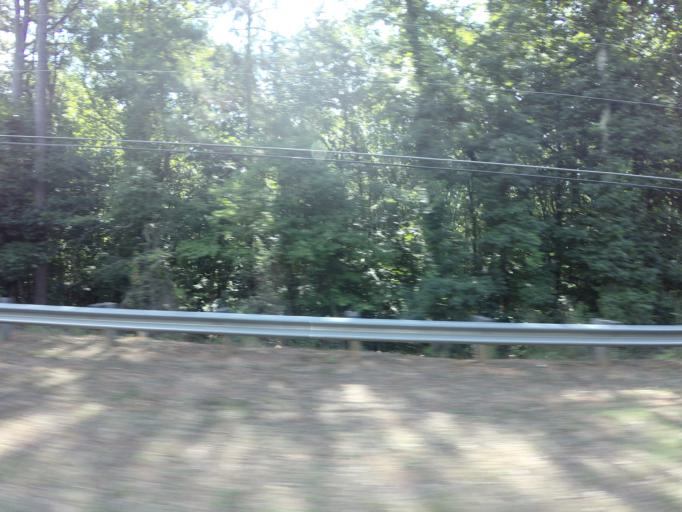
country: US
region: Georgia
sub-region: Fulton County
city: Johns Creek
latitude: 34.0353
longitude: -84.1634
